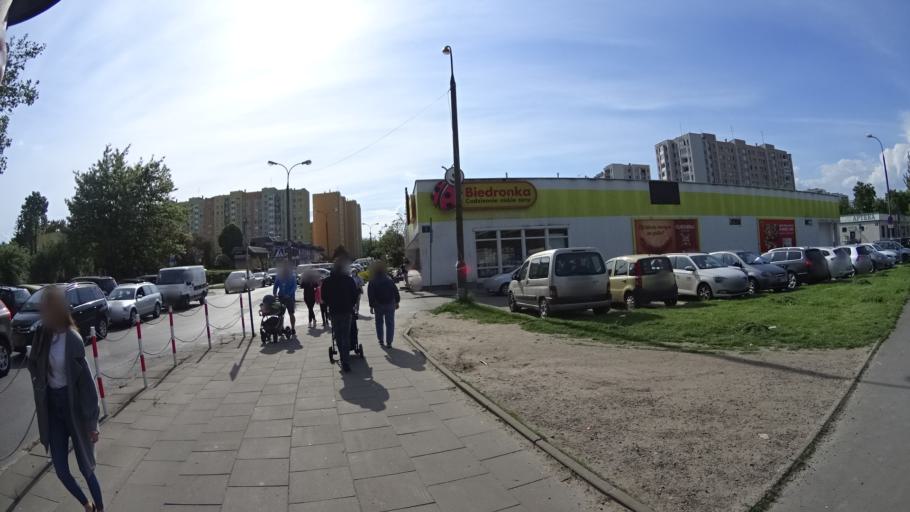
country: PL
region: Masovian Voivodeship
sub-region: Warszawa
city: Bemowo
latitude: 52.2368
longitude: 20.9126
